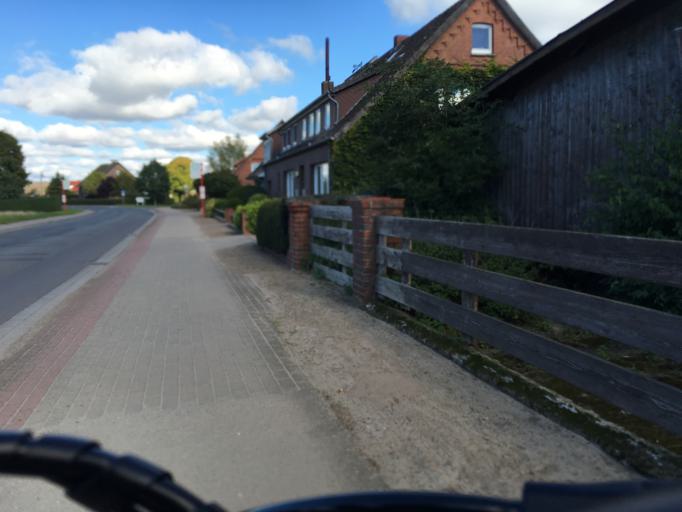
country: DE
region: Lower Saxony
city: Bardowick
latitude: 53.3050
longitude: 10.3881
